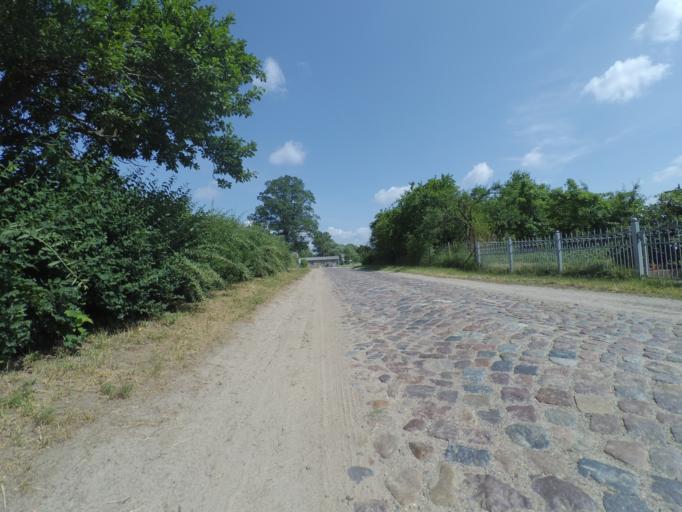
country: DE
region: Mecklenburg-Vorpommern
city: Plau am See
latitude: 53.4301
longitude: 12.1615
